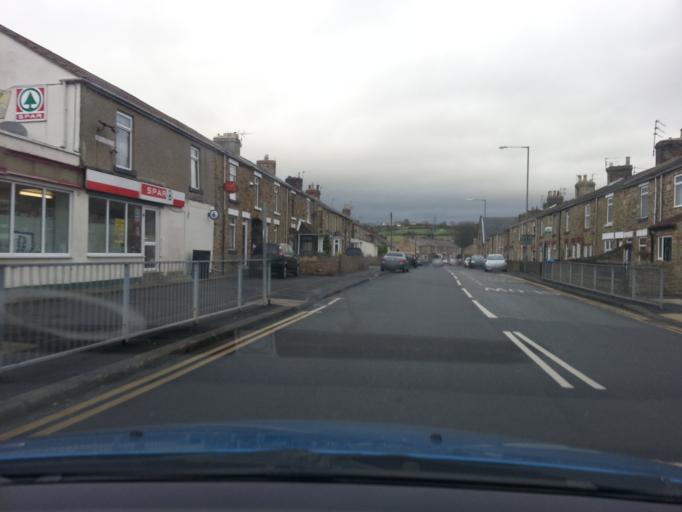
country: GB
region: England
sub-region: County Durham
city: Crook
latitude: 54.6951
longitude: -1.7494
